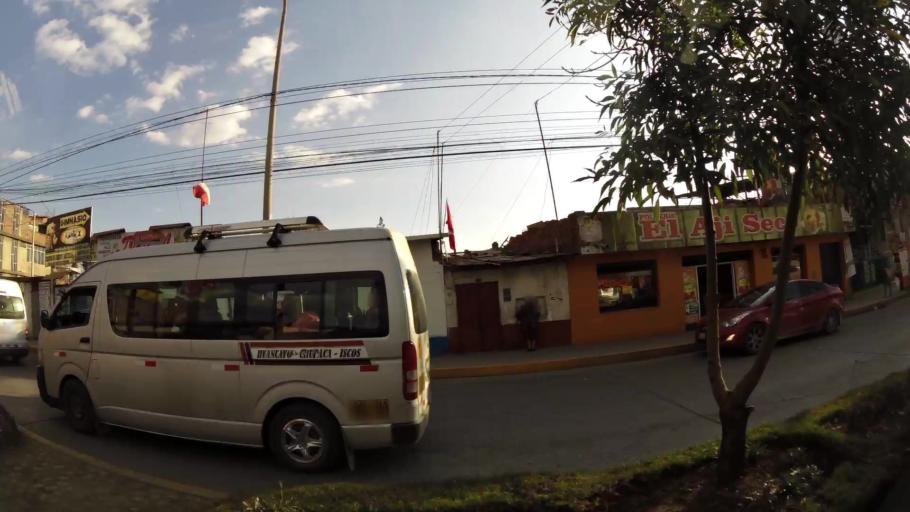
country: PE
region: Junin
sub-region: Provincia de Huancayo
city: El Tambo
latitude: -12.0499
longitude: -75.2219
